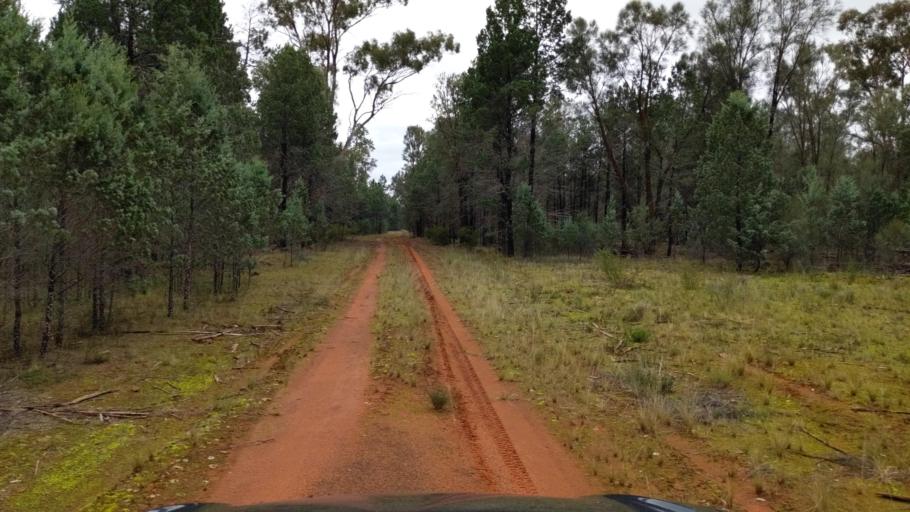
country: AU
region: New South Wales
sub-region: Coolamon
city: Coolamon
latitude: -34.8487
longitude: 146.9322
